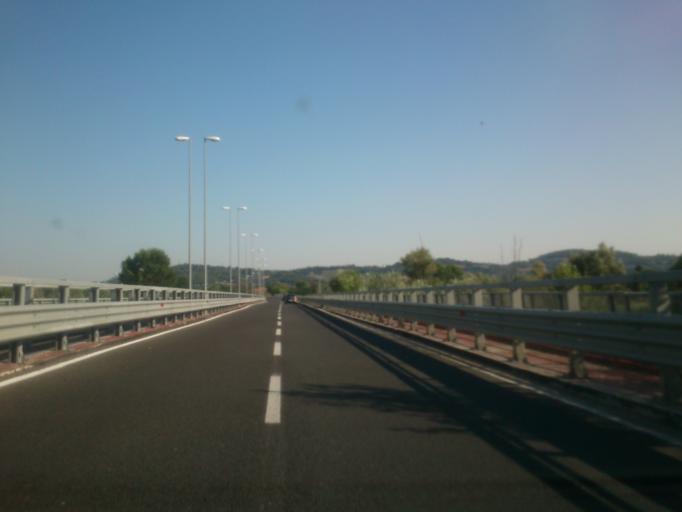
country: IT
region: The Marches
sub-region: Provincia di Pesaro e Urbino
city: Pesaro
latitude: 43.9043
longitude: 12.8718
